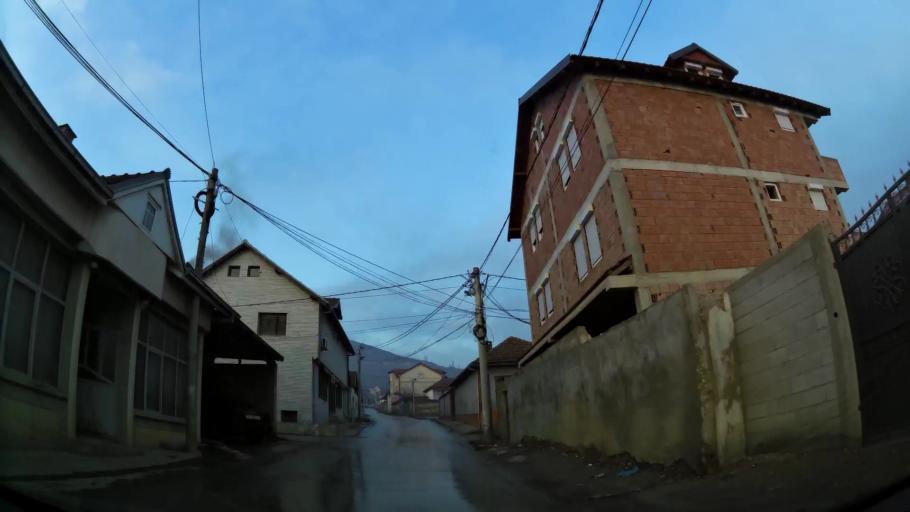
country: MK
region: Aracinovo
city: Arachinovo
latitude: 42.0300
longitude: 21.5654
